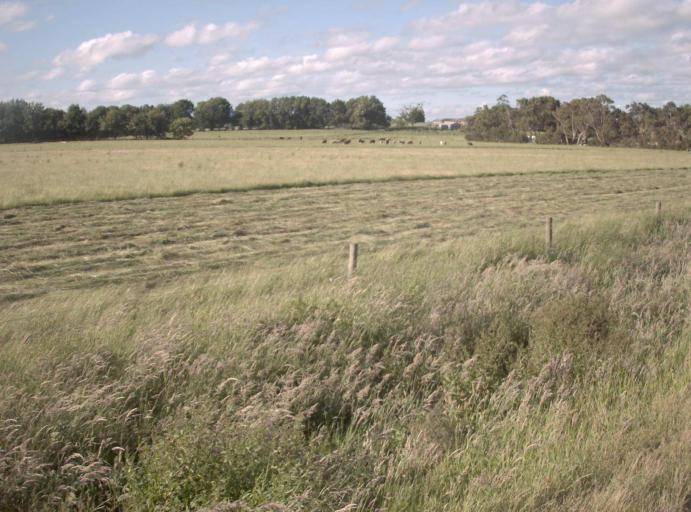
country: AU
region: Victoria
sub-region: Bass Coast
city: North Wonthaggi
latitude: -38.5087
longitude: 145.9081
